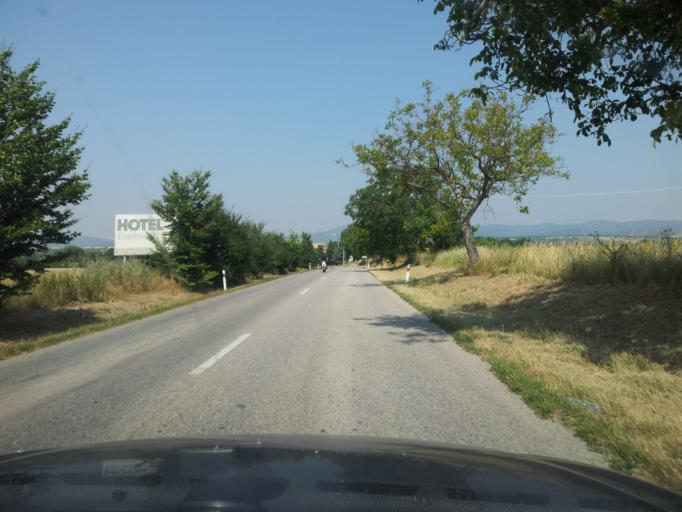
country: SK
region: Nitriansky
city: Zlate Moravce
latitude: 48.3780
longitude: 18.4085
